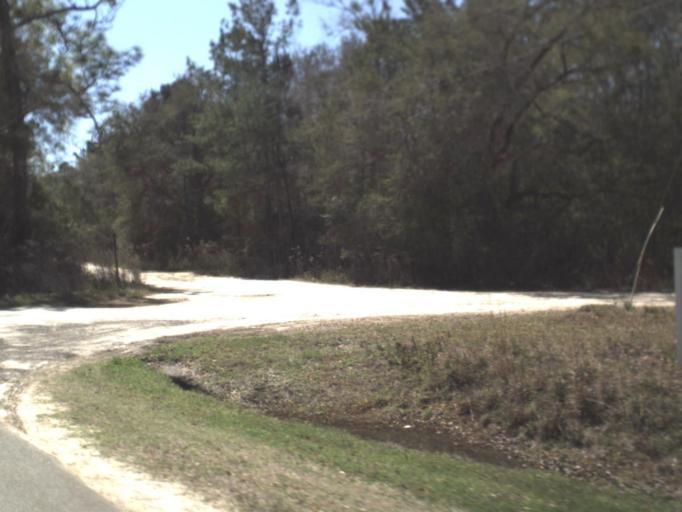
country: US
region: Florida
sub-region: Leon County
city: Woodville
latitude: 30.2145
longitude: -84.2238
